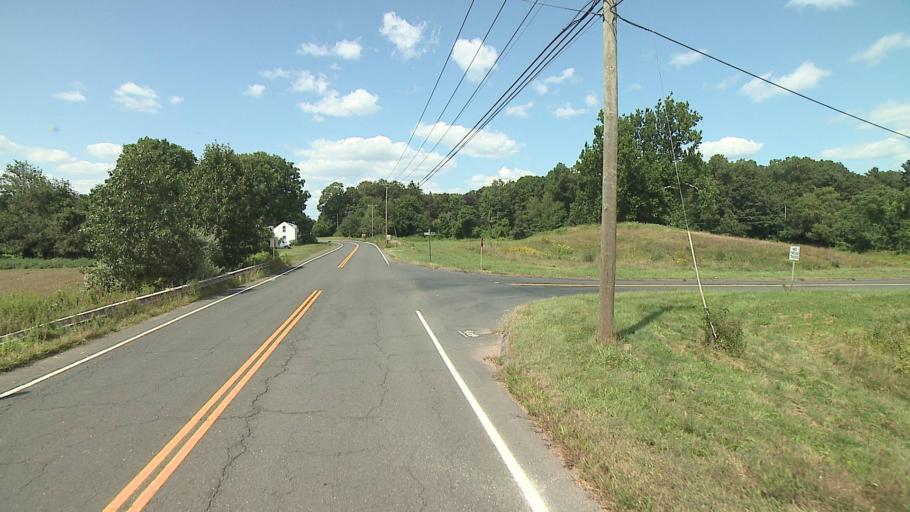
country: US
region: Connecticut
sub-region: Hartford County
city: Broad Brook
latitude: 41.9362
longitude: -72.5123
